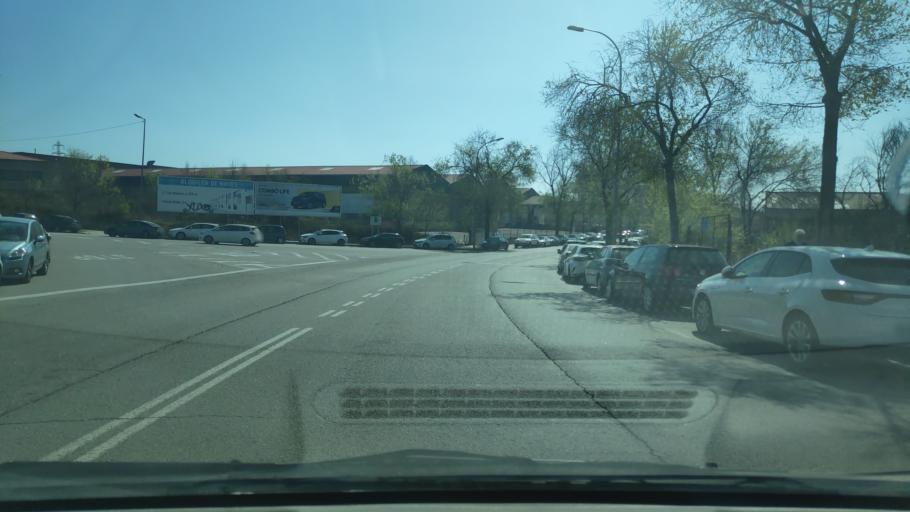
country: ES
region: Catalonia
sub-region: Provincia de Barcelona
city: Sabadell
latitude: 41.5446
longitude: 2.1294
